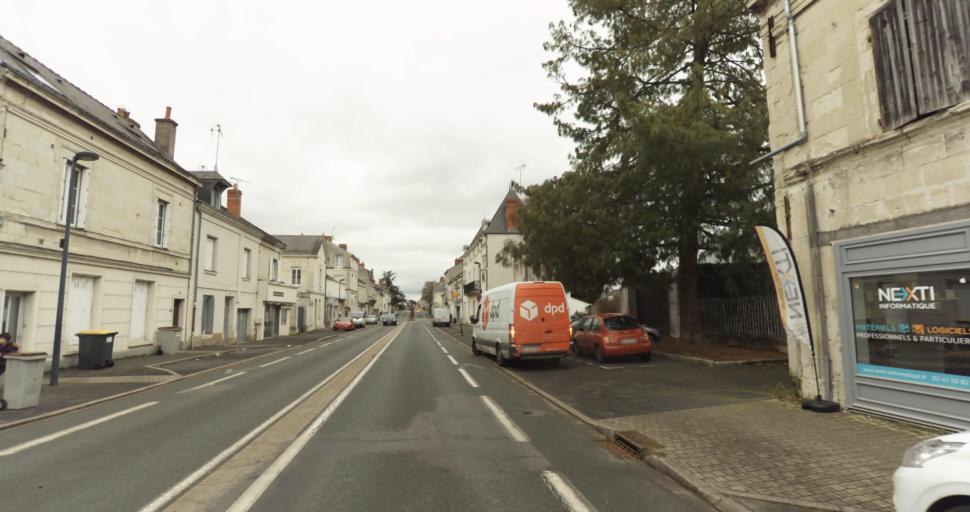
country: FR
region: Pays de la Loire
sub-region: Departement de Maine-et-Loire
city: Saumur
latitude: 47.2506
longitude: -0.0890
